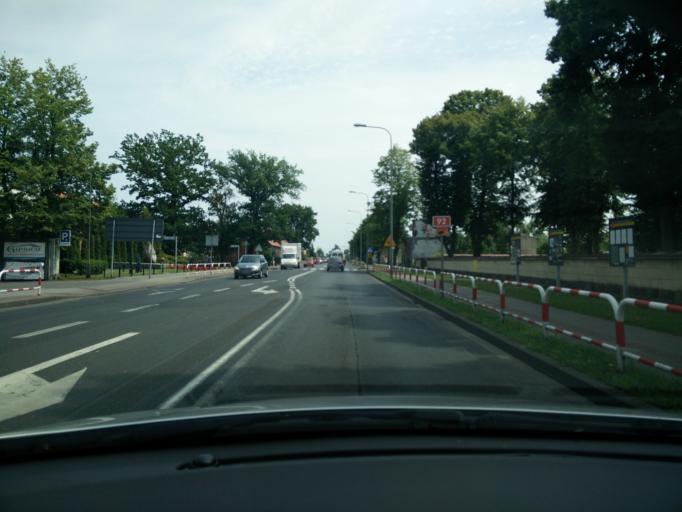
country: PL
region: Greater Poland Voivodeship
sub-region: Powiat slupecki
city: Strzalkowo
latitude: 52.3097
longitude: 17.8188
